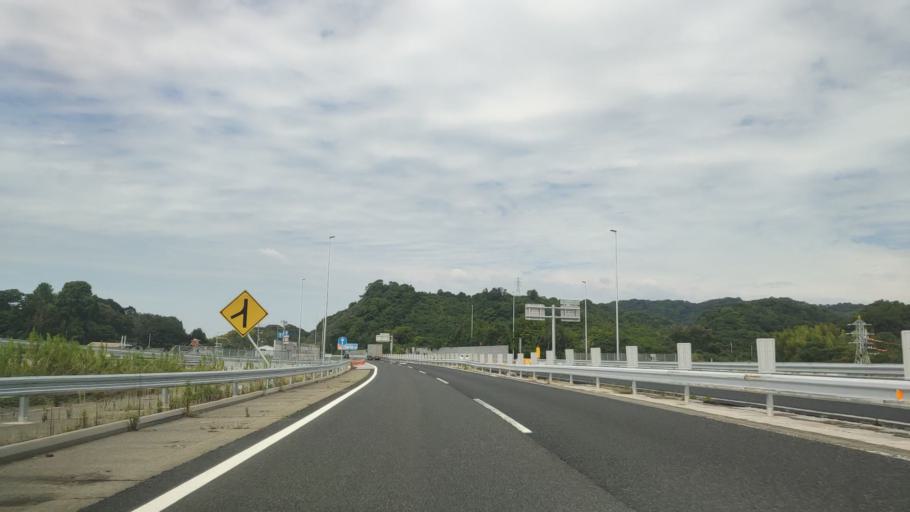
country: JP
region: Wakayama
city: Wakayama-shi
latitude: 34.2089
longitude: 135.2285
